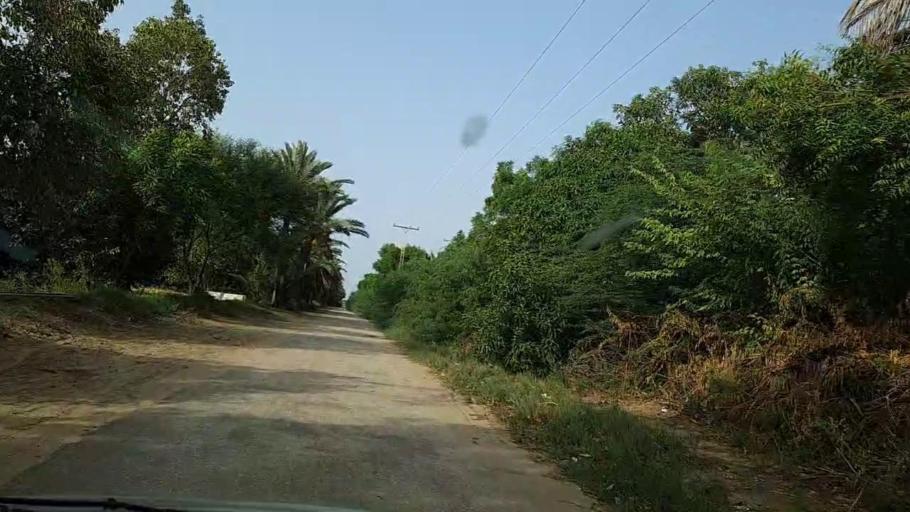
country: PK
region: Sindh
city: Kotri
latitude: 25.2253
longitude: 68.2515
